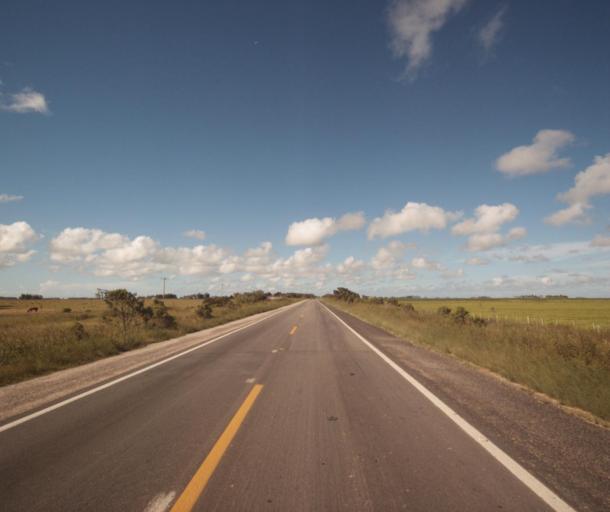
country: UY
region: Cerro Largo
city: Rio Branco
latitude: -33.0415
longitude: -52.8629
